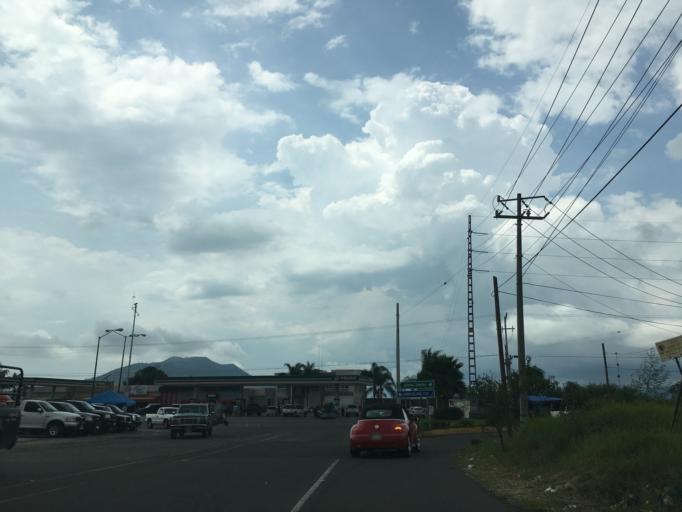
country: MX
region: Michoacan
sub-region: Periban
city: Gildardo Magana (Los Angeles)
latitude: 19.5773
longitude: -102.4781
